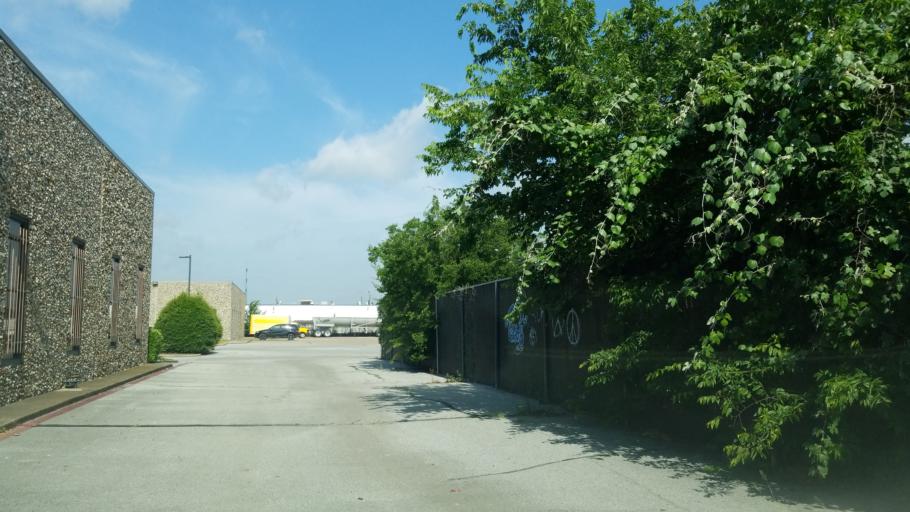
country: US
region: Texas
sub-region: Dallas County
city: Farmers Branch
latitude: 32.8804
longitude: -96.8883
